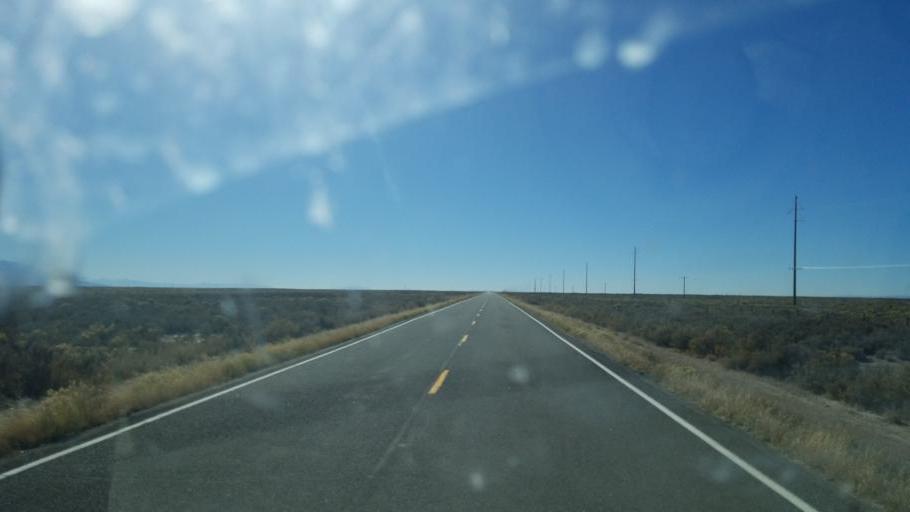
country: US
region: Colorado
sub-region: Saguache County
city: Center
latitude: 37.9327
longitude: -105.9012
